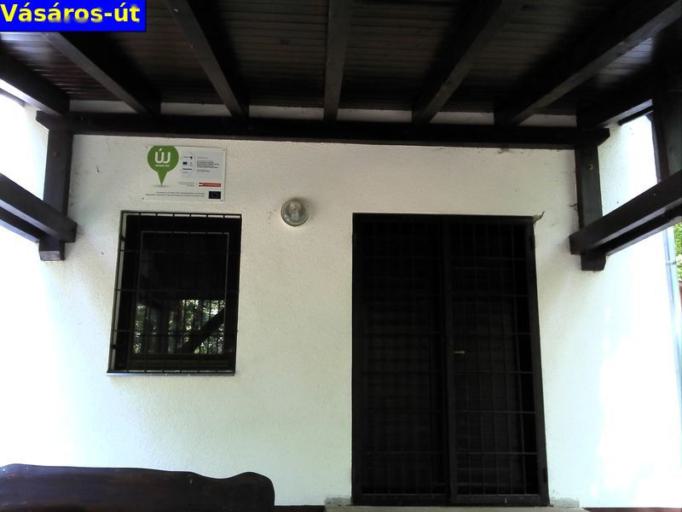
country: HU
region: Baranya
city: Pellerd
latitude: 46.1129
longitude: 18.1367
